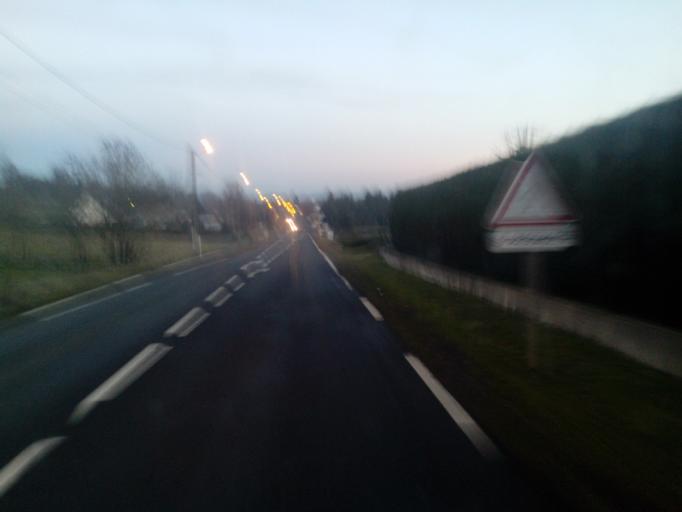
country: FR
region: Auvergne
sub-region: Departement du Cantal
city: Murat
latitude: 45.0833
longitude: 2.9304
